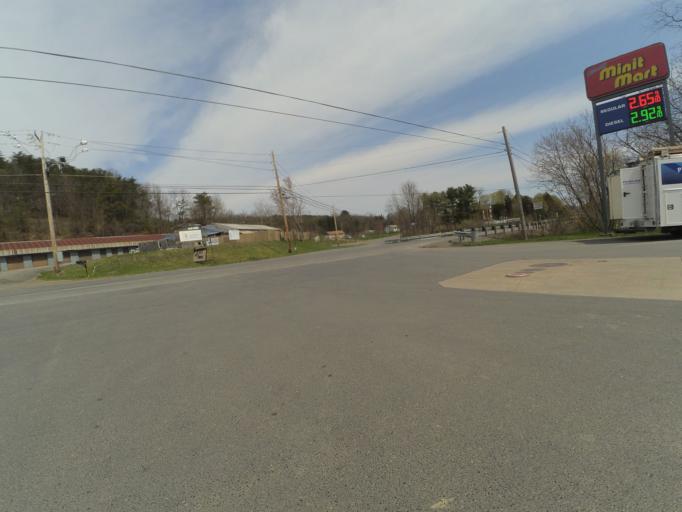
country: US
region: Pennsylvania
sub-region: Clinton County
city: Avis
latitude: 41.1802
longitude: -77.3299
